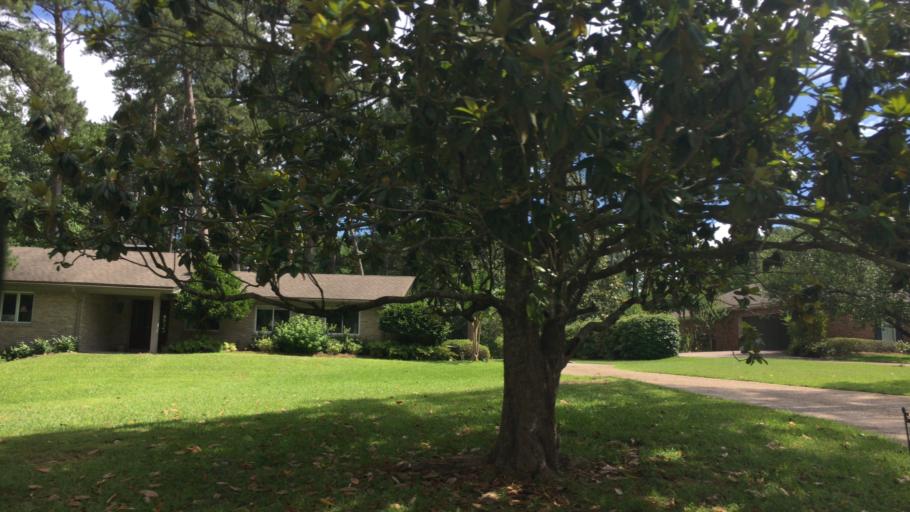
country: US
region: Louisiana
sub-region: Lincoln Parish
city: Ruston
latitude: 32.5503
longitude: -92.6330
